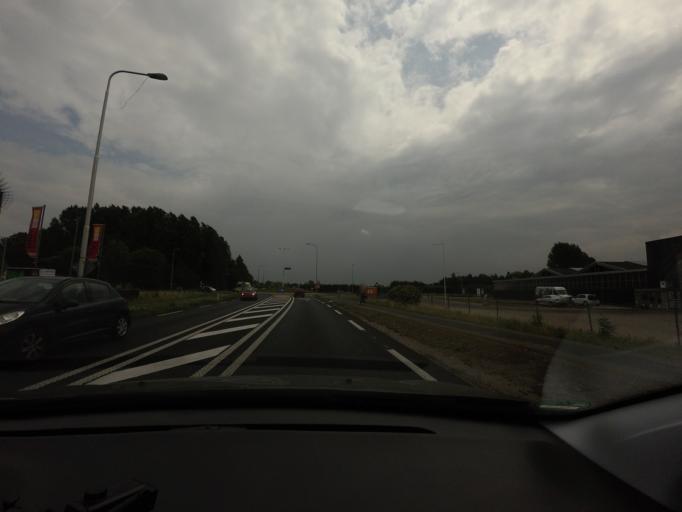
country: NL
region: Gelderland
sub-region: Gemeente Tiel
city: Tiel
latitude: 51.8886
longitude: 5.3885
